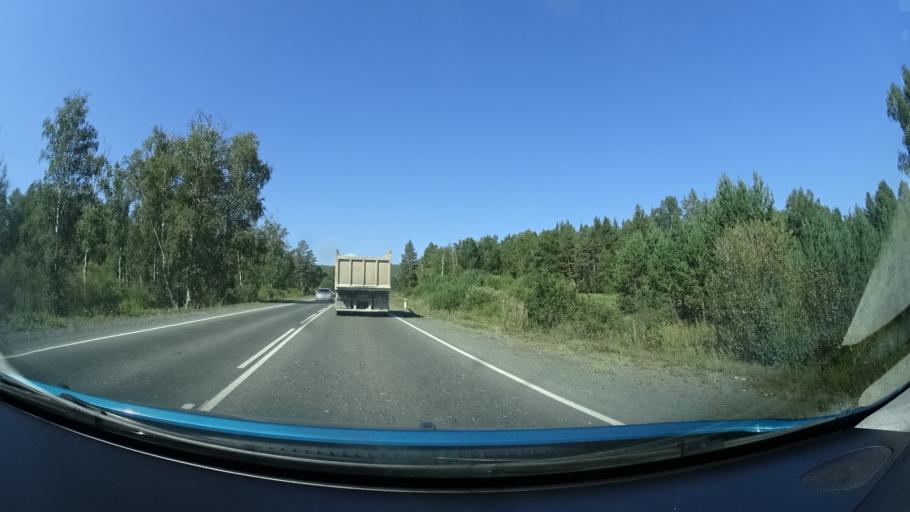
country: RU
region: Bashkortostan
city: Abzakovo
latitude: 53.8616
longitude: 58.5496
